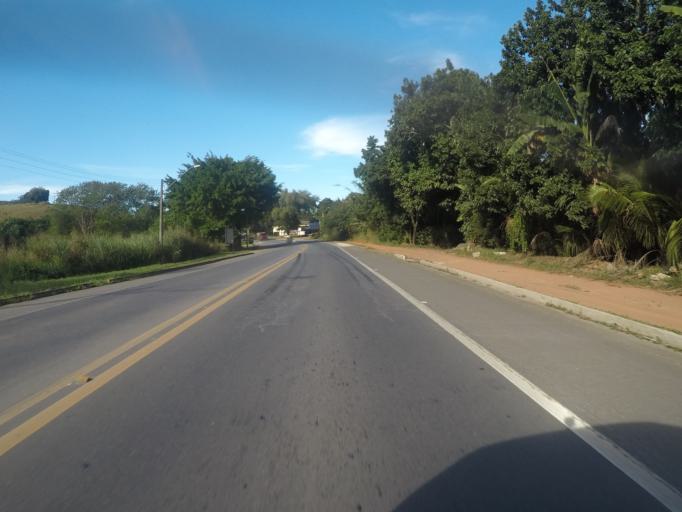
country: BR
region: Espirito Santo
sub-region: Ibiracu
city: Ibiracu
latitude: -19.8682
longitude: -40.4069
